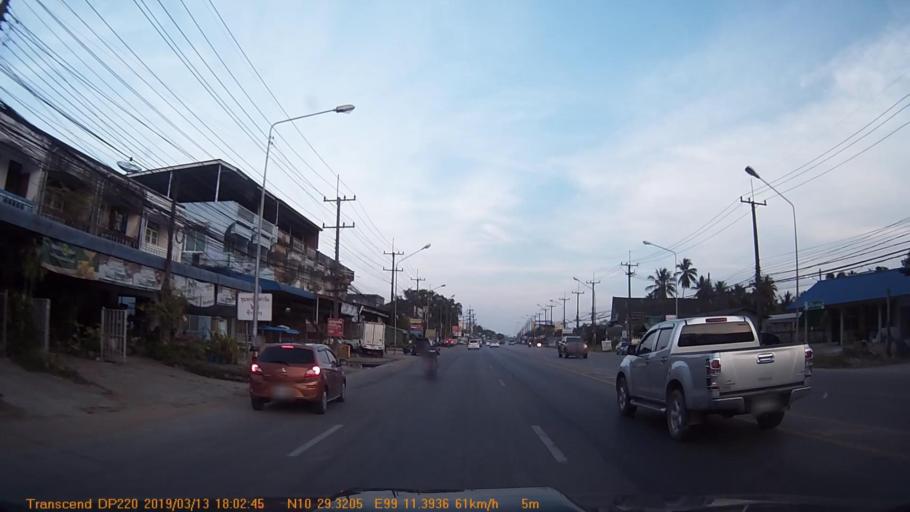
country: TH
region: Chumphon
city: Chumphon
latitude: 10.4886
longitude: 99.1901
